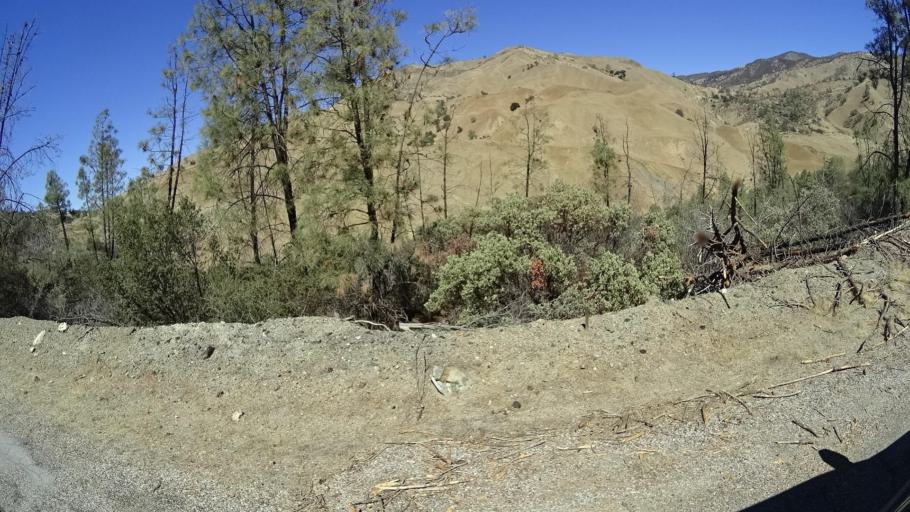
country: US
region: California
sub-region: Monterey County
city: King City
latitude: 36.2916
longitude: -120.8774
